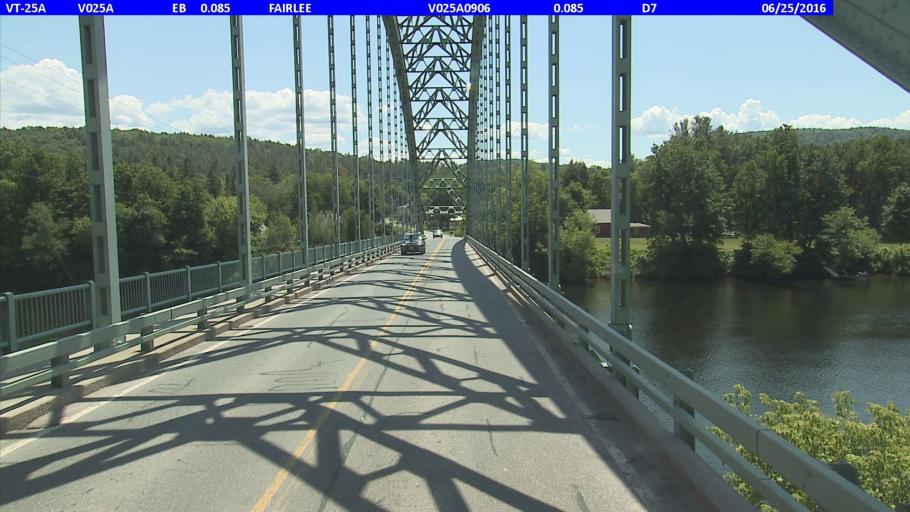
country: US
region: New Hampshire
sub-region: Grafton County
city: Orford
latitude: 43.9076
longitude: -72.1400
